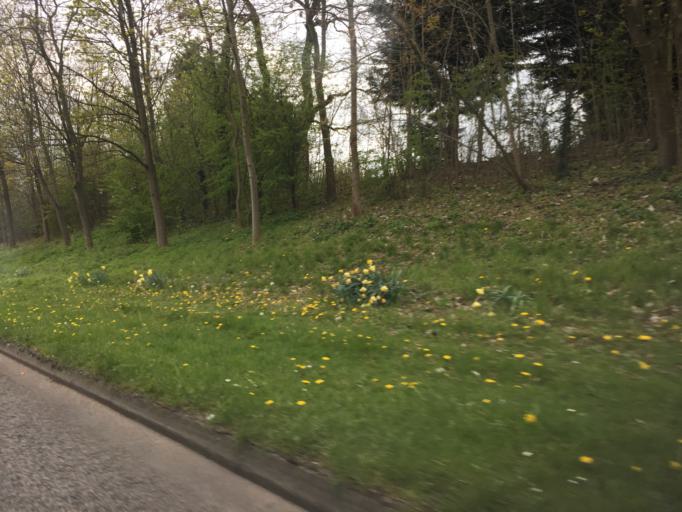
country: GB
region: England
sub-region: Milton Keynes
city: Milton Keynes
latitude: 52.0474
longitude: -0.7655
